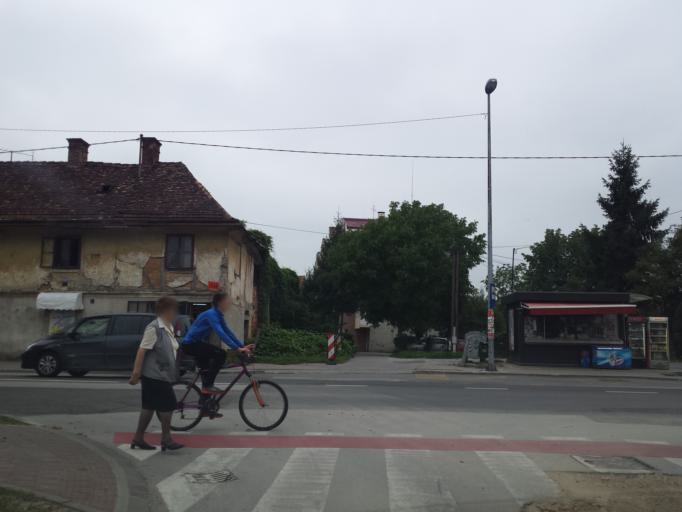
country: HR
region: Karlovacka
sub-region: Grad Karlovac
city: Karlovac
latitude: 45.4919
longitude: 15.5418
